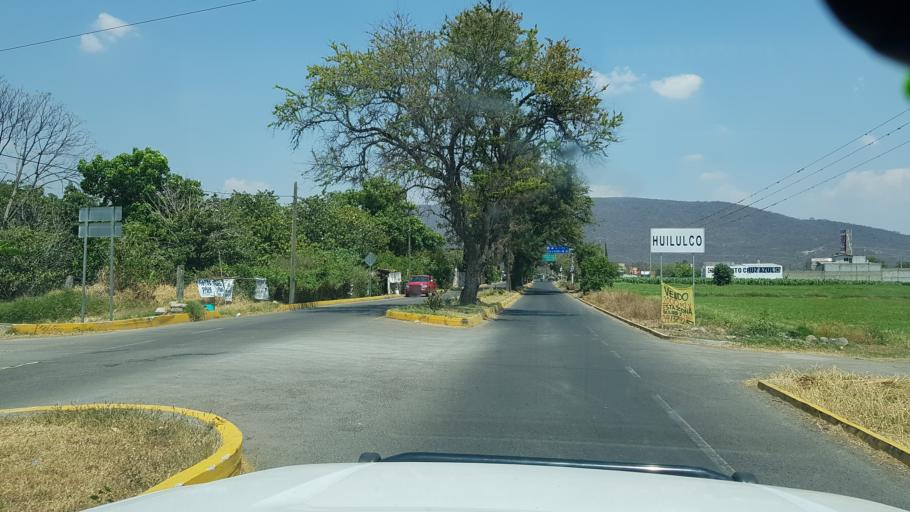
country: MX
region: Puebla
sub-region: Huaquechula
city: Cacaloxuchitl
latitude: 18.7905
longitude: -98.4568
